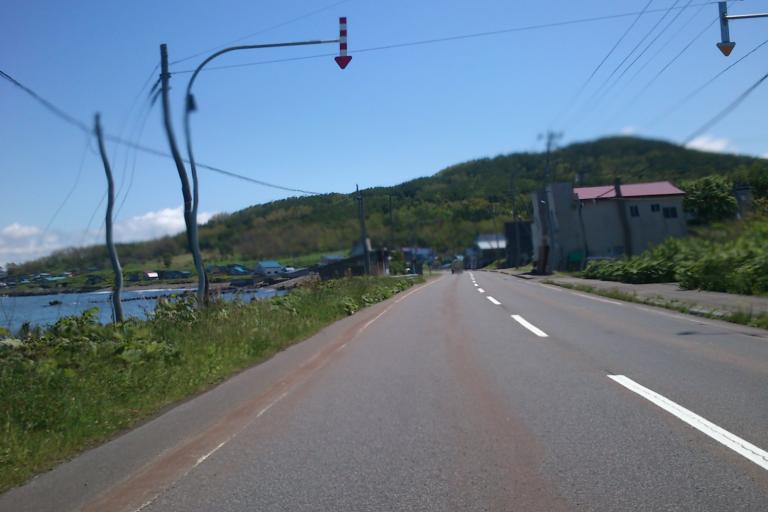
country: JP
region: Hokkaido
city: Rumoi
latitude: 43.8355
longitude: 141.4889
